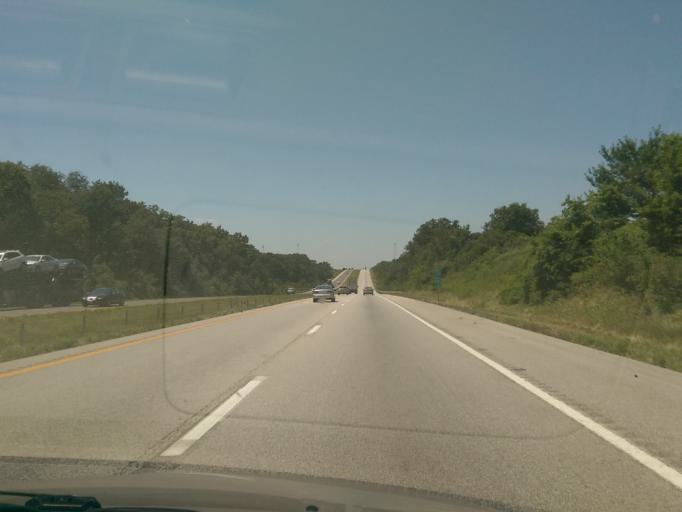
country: US
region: Missouri
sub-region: Saline County
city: Marshall
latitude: 38.9483
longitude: -93.0155
